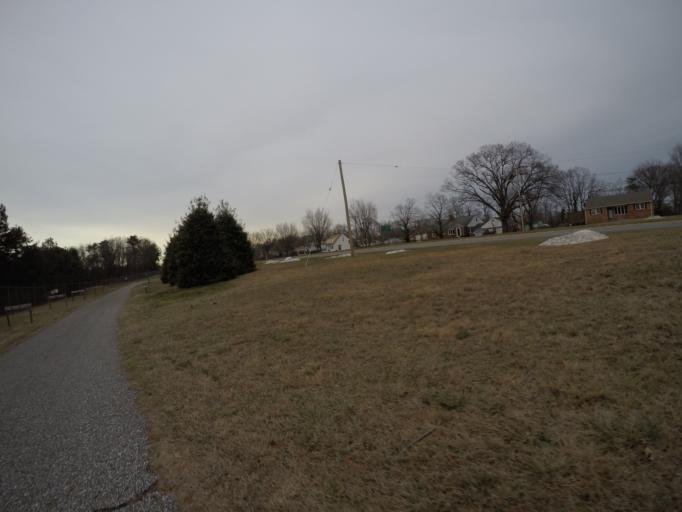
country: US
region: Maryland
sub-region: Anne Arundel County
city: Ferndale
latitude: 39.1841
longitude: -76.6530
